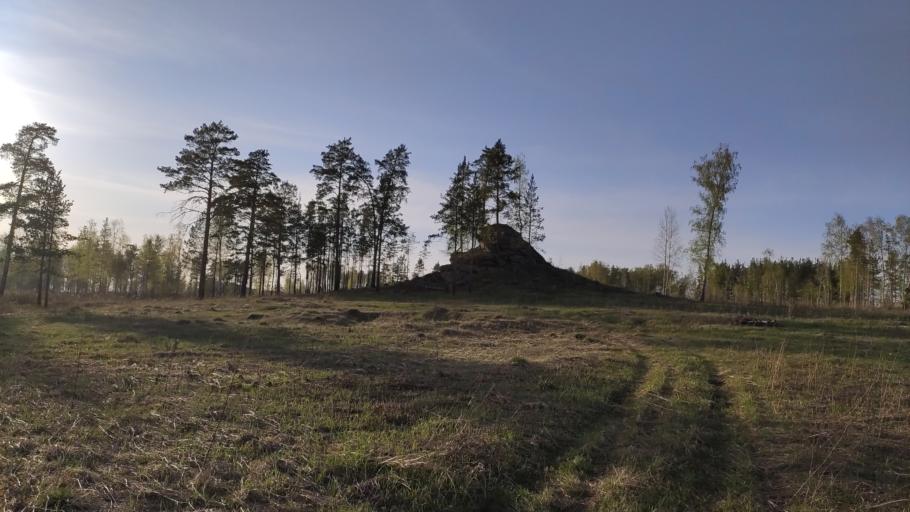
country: RU
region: Sverdlovsk
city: Shabrovskiy
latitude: 56.6564
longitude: 60.6348
